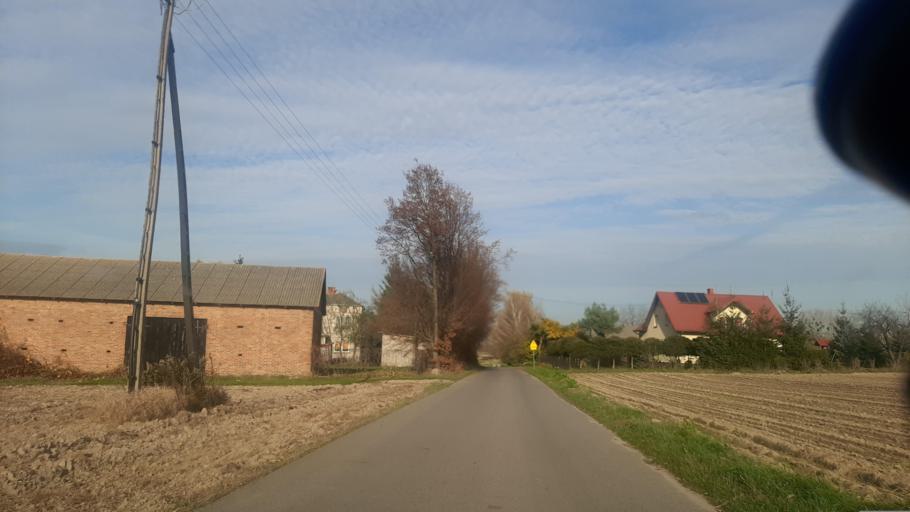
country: PL
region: Lublin Voivodeship
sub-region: Powiat pulawski
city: Markuszow
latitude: 51.3859
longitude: 22.2903
